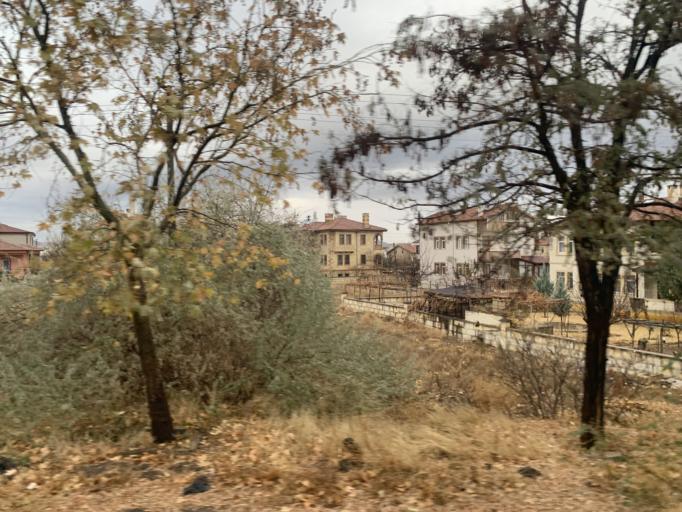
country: TR
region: Nevsehir
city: Avanos
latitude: 38.7085
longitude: 34.8578
